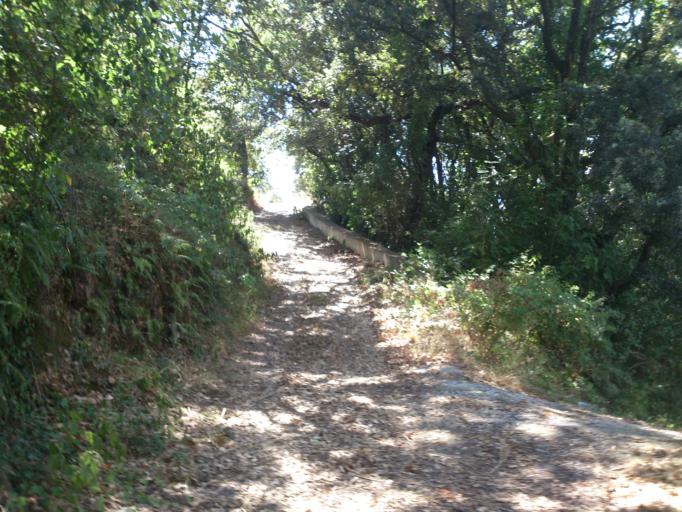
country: IT
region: Calabria
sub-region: Provincia di Reggio Calabria
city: Pazzano
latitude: 38.4758
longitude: 16.4485
